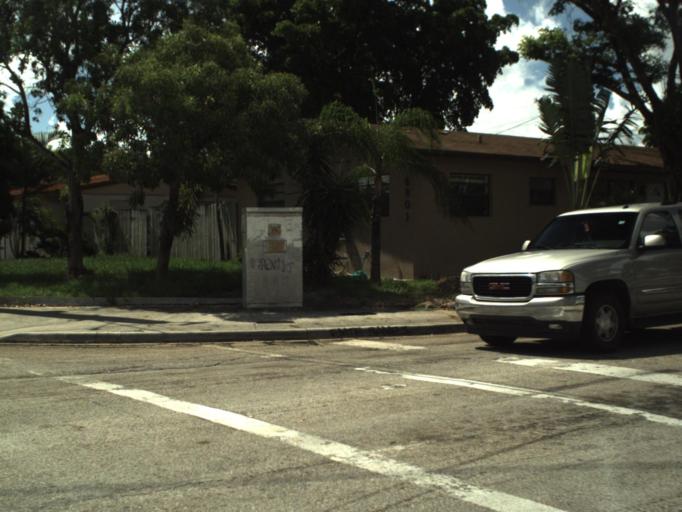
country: US
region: Florida
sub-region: Broward County
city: Pembroke Pines
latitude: 26.0318
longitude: -80.2245
